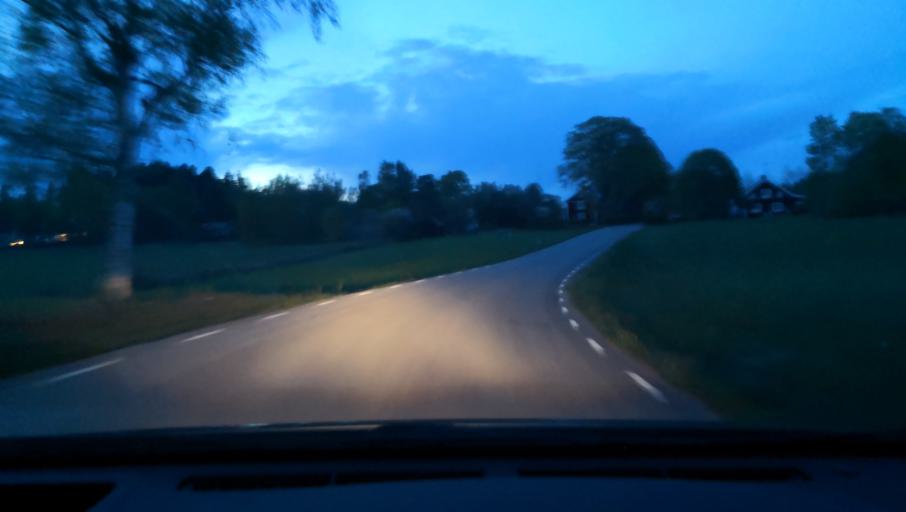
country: SE
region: OErebro
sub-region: Orebro Kommun
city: Vintrosa
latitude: 59.1795
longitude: 15.0186
